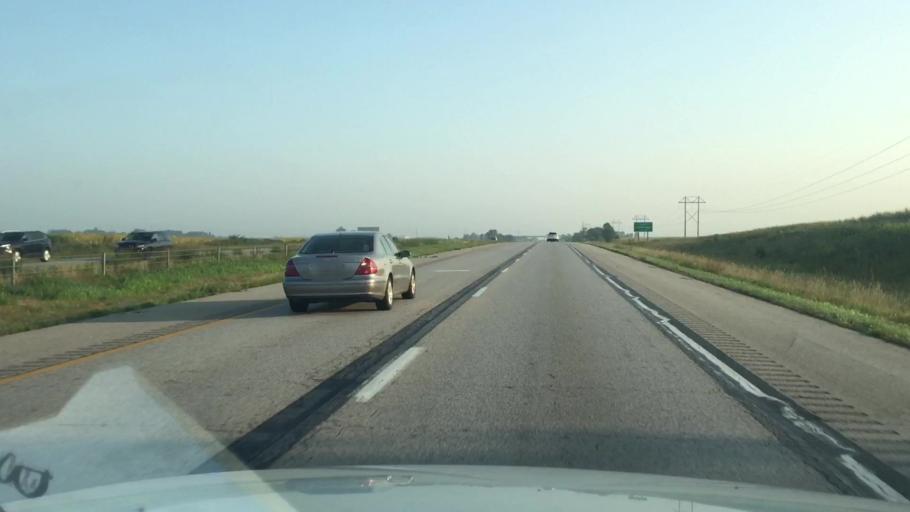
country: US
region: Iowa
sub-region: Story County
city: Huxley
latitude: 41.8639
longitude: -93.5709
